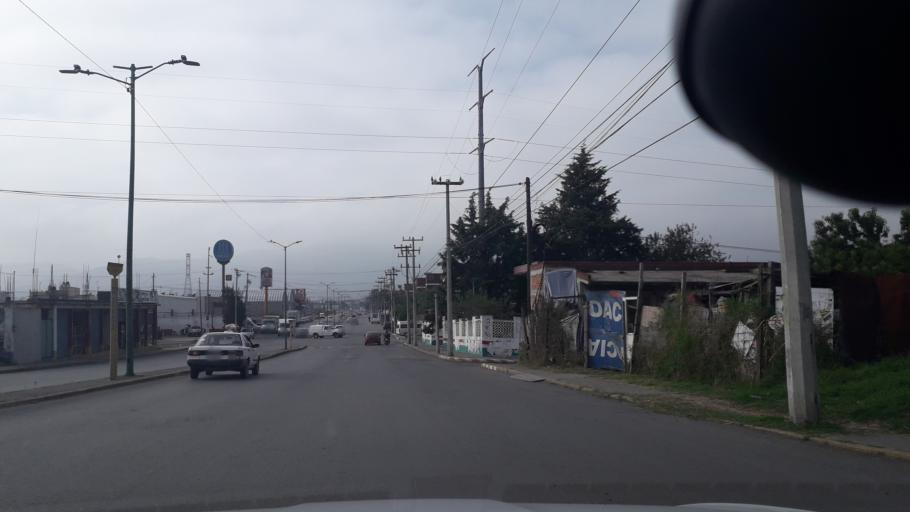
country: MX
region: Mexico
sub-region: Jaltenco
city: Alborada Jaltenco
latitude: 19.6457
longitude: -99.0778
